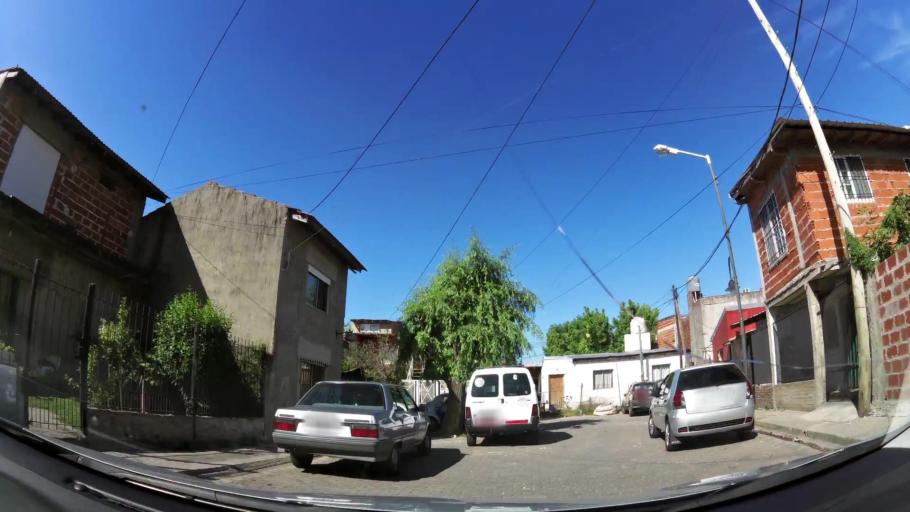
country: AR
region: Buenos Aires
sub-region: Partido de Tigre
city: Tigre
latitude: -34.4757
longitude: -58.5813
